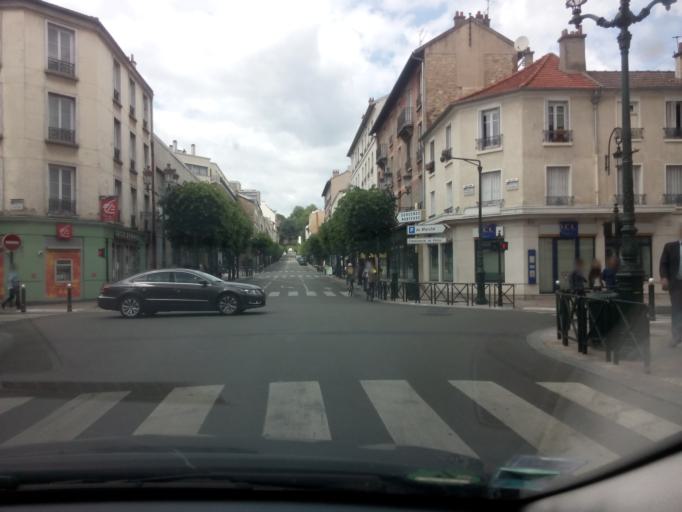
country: FR
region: Ile-de-France
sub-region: Departement des Hauts-de-Seine
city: Puteaux
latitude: 48.8808
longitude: 2.2380
